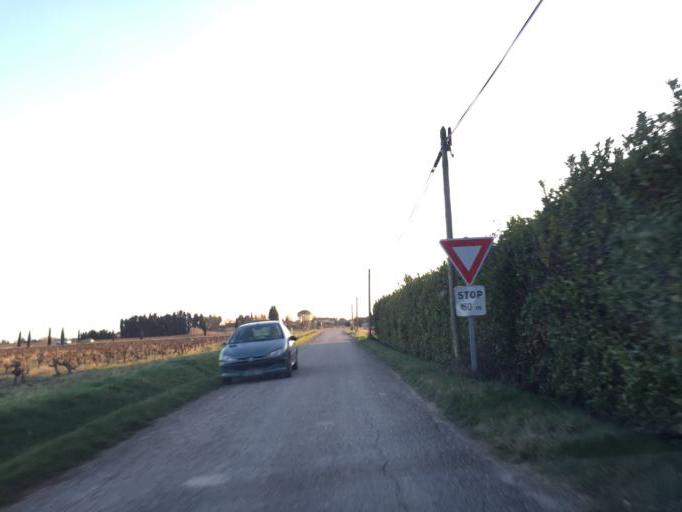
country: FR
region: Provence-Alpes-Cote d'Azur
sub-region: Departement du Vaucluse
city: Camaret-sur-Aigues
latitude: 44.1551
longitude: 4.8719
